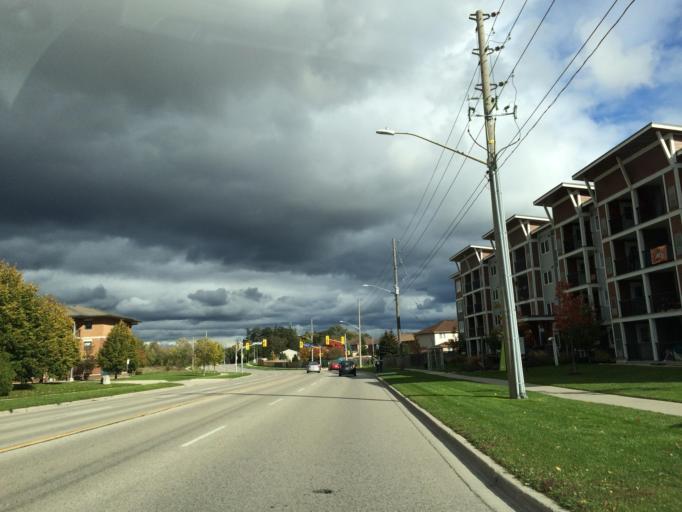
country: CA
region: Ontario
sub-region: Wellington County
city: Guelph
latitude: 43.5289
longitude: -80.2796
